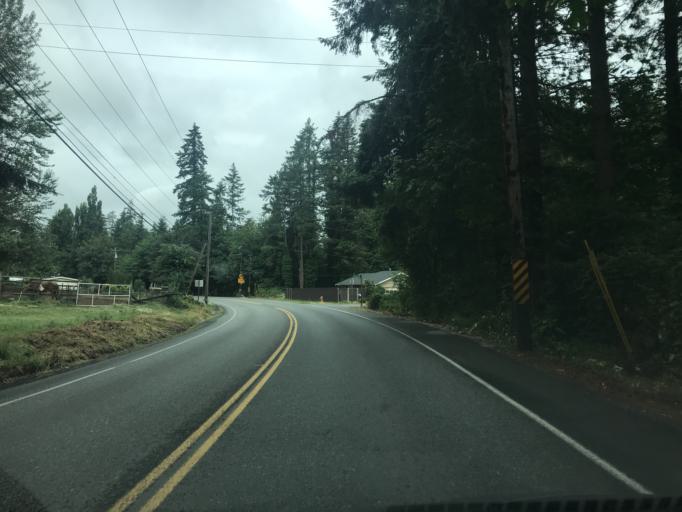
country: US
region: Washington
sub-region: King County
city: Covington
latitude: 47.3481
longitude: -122.1097
